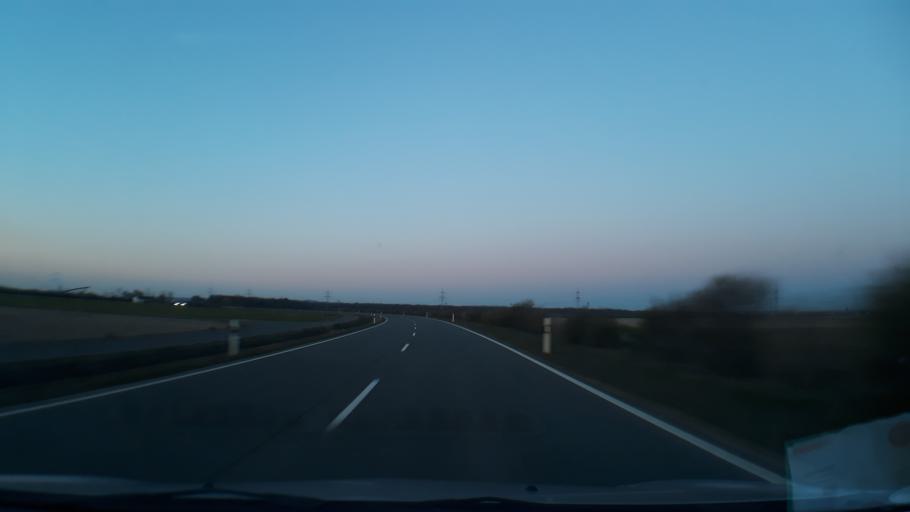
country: DE
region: North Rhine-Westphalia
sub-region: Regierungsbezirk Koln
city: Kerpen
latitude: 50.8681
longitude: 6.6345
